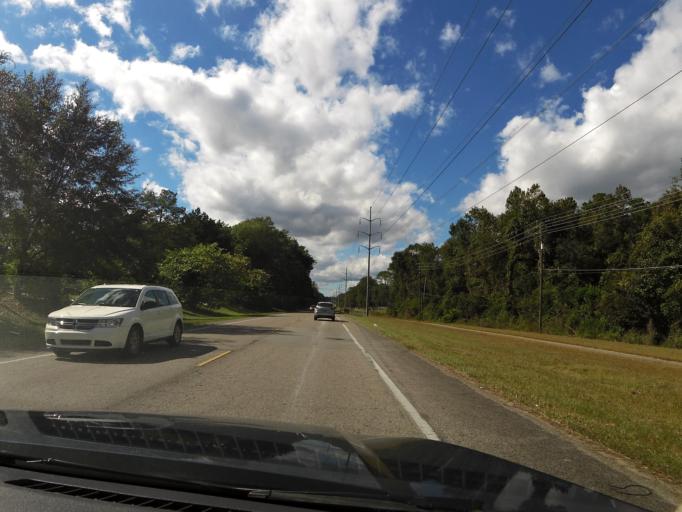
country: US
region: Florida
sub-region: Alachua County
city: Gainesville
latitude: 29.7034
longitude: -82.3706
